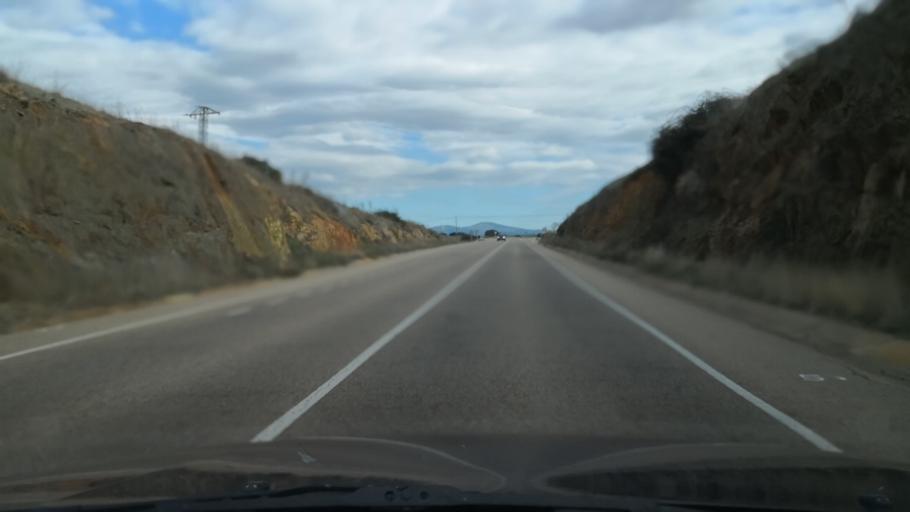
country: ES
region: Castille and Leon
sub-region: Provincia de Salamanca
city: Herguijuela de Ciudad Rodrigo
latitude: 40.4836
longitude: -6.5808
